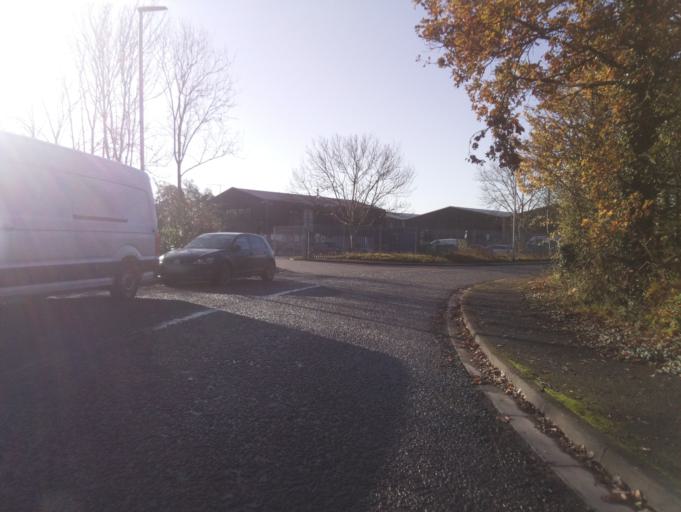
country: GB
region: England
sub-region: Somerset
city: Puriton
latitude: 51.1651
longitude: -2.9849
